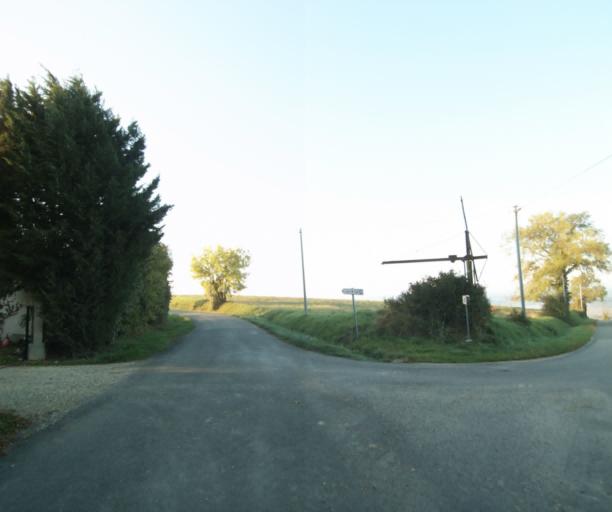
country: FR
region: Midi-Pyrenees
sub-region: Departement du Gers
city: Eauze
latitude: 43.7794
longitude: 0.1759
